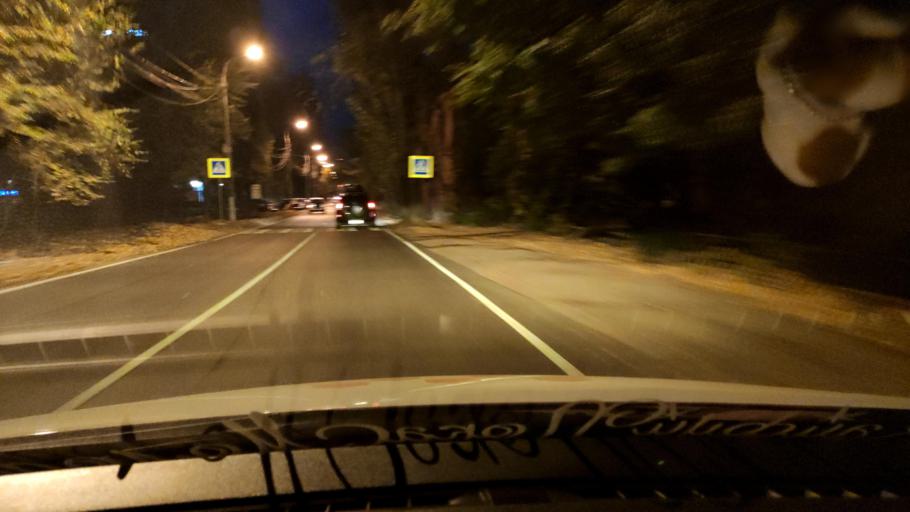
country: RU
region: Voronezj
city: Voronezh
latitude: 51.6779
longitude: 39.1655
